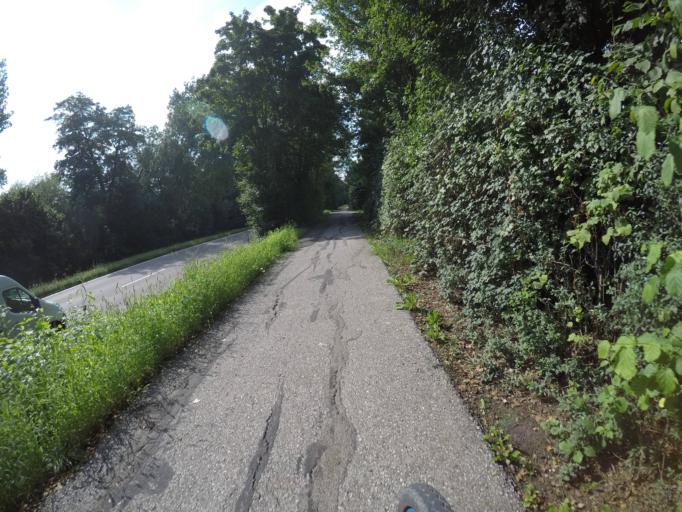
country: DE
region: Baden-Wuerttemberg
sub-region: Regierungsbezirk Stuttgart
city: Unterensingen
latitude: 48.6573
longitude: 9.3634
